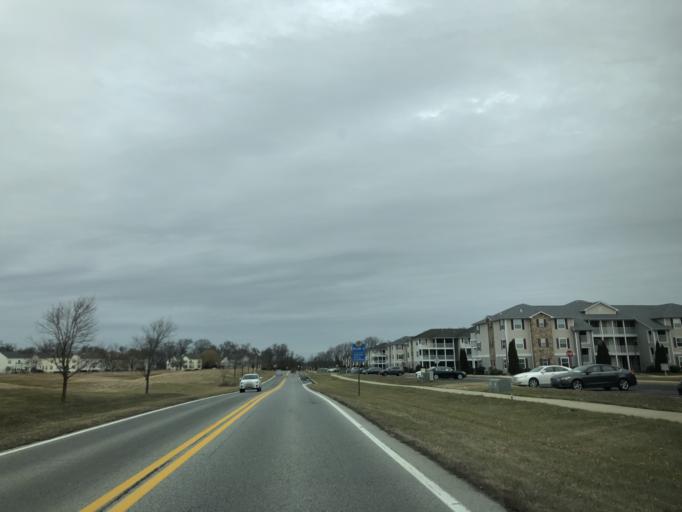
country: US
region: Delaware
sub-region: New Castle County
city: Middletown
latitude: 39.4681
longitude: -75.7105
